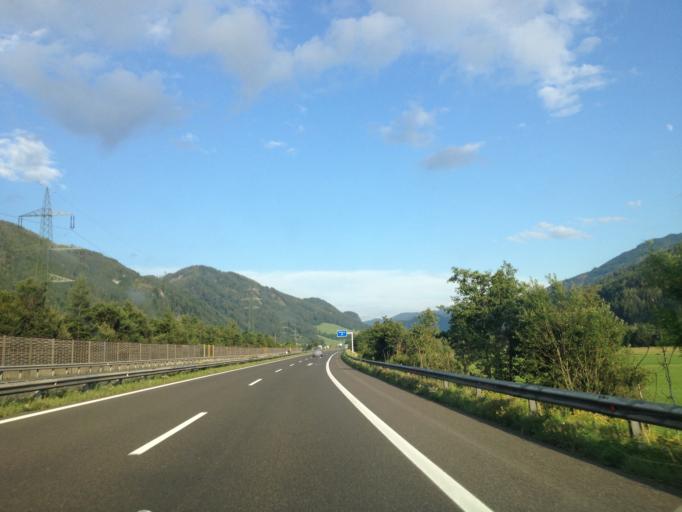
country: AT
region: Styria
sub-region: Politischer Bezirk Leoben
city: Kalwang
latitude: 47.4277
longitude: 14.7434
